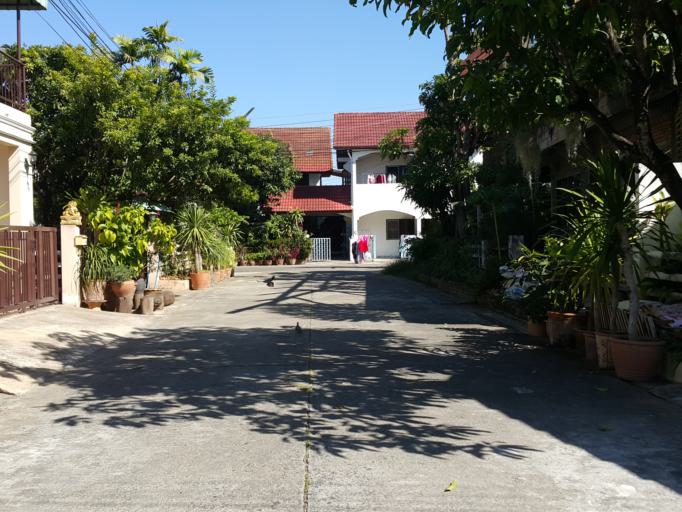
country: TH
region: Chiang Mai
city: Chiang Mai
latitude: 18.7797
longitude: 99.0300
